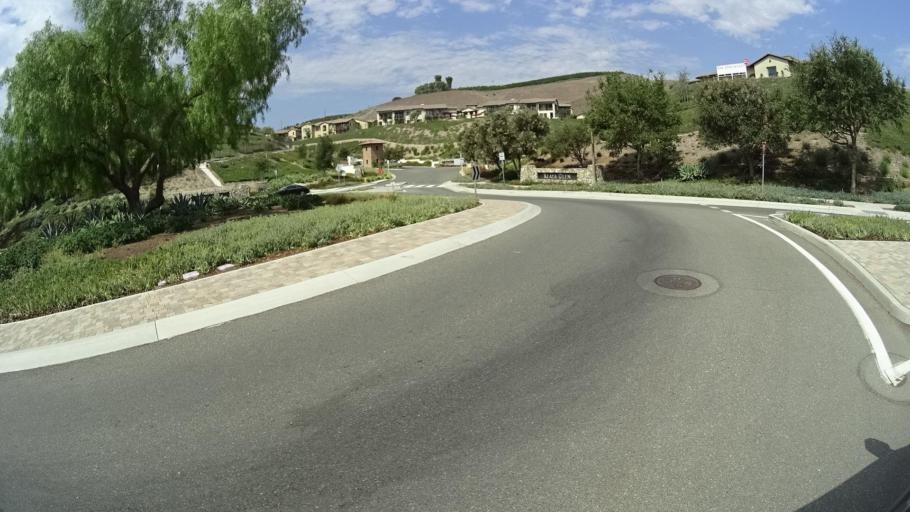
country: US
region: California
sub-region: Orange County
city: San Juan Capistrano
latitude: 33.5217
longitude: -117.6276
